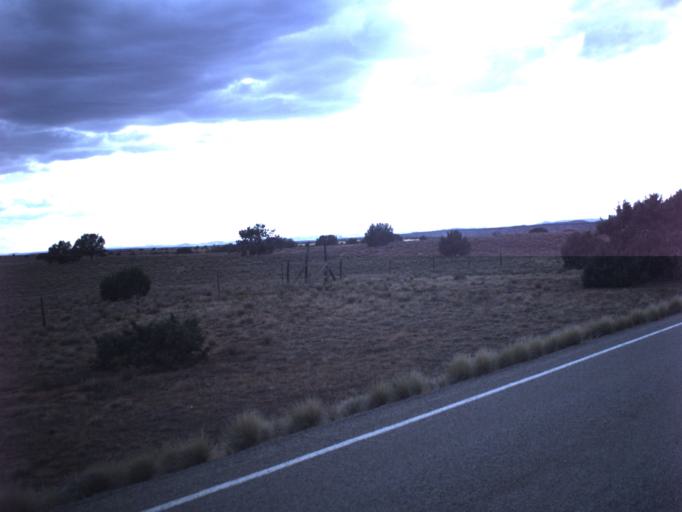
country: US
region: Utah
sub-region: San Juan County
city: Blanding
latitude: 37.4354
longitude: -109.3800
